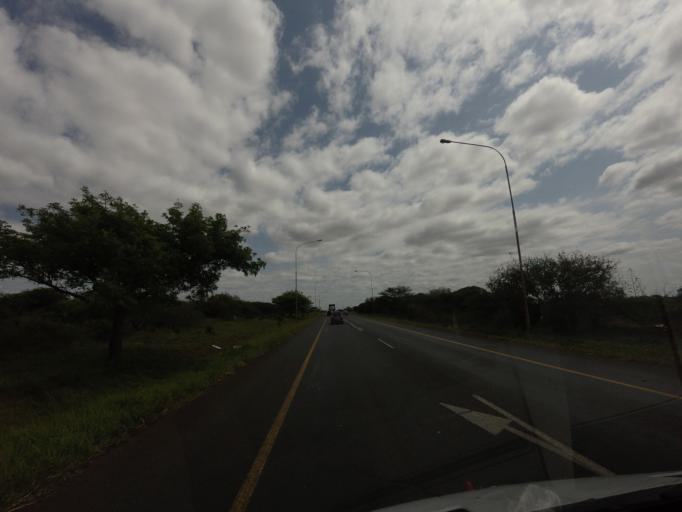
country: ZA
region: KwaZulu-Natal
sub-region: uMkhanyakude District Municipality
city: Hluhluwe
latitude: -28.0933
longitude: 32.2687
